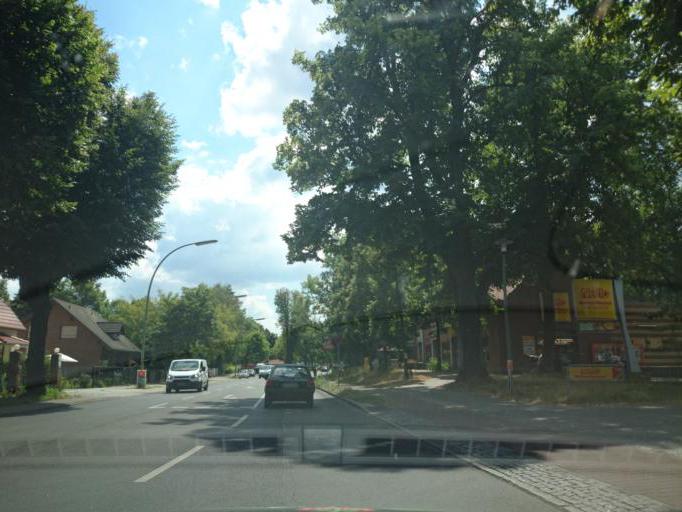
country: DE
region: Berlin
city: Gatow
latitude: 52.4858
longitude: 13.1828
